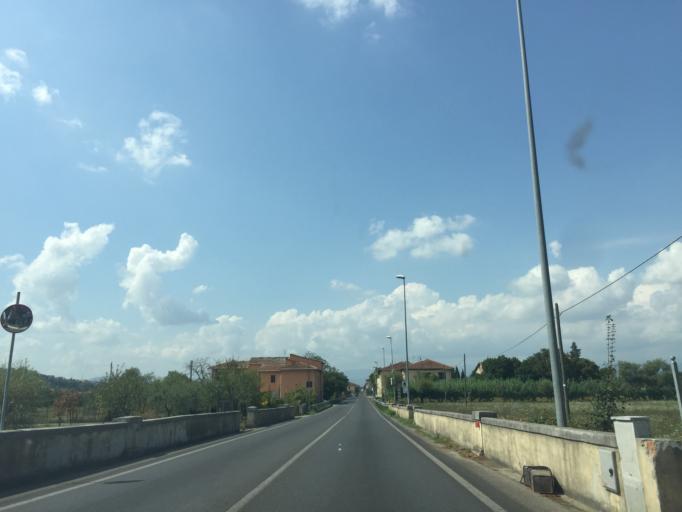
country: IT
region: Tuscany
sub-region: Provincia di Prato
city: Seano
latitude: 43.8377
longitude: 11.0242
